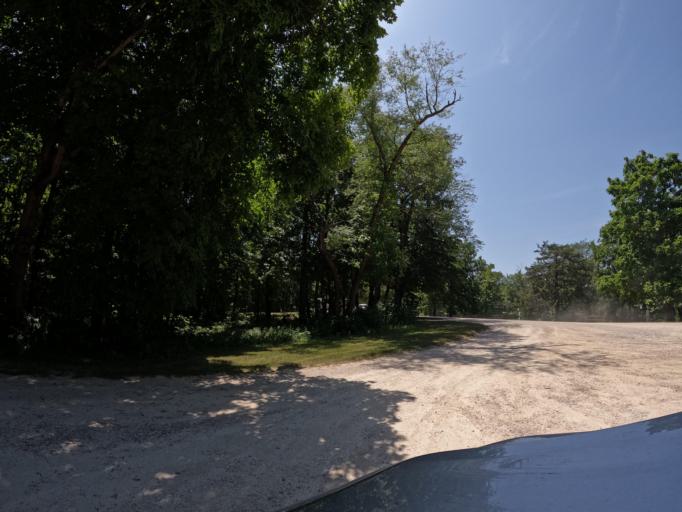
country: US
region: Iowa
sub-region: Henry County
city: Mount Pleasant
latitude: 40.9323
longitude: -91.6152
